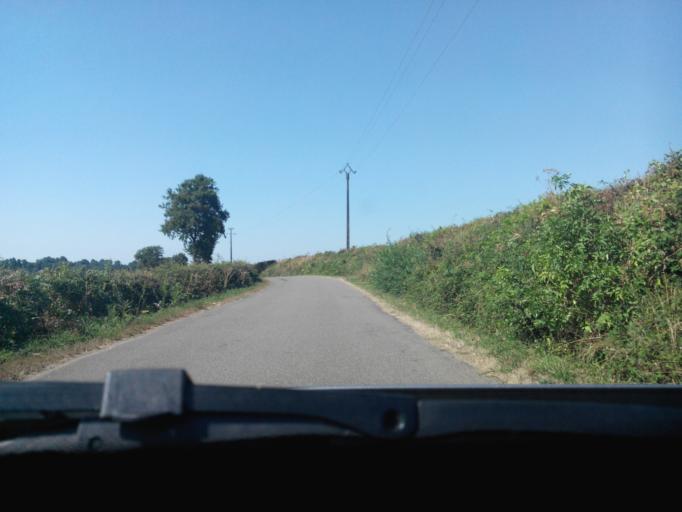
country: FR
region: Poitou-Charentes
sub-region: Departement de la Charente
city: Brigueuil
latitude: 45.9696
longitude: 0.7953
